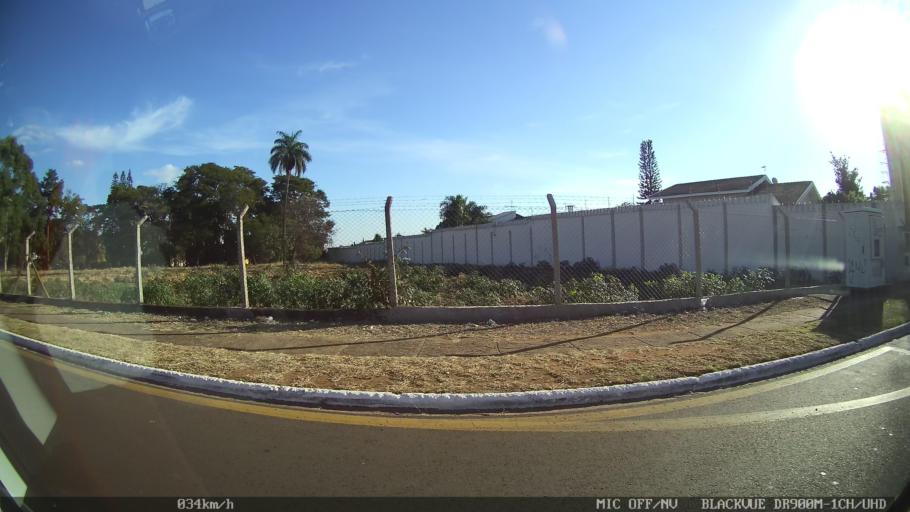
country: BR
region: Sao Paulo
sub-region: Franca
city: Franca
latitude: -20.5188
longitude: -47.3714
